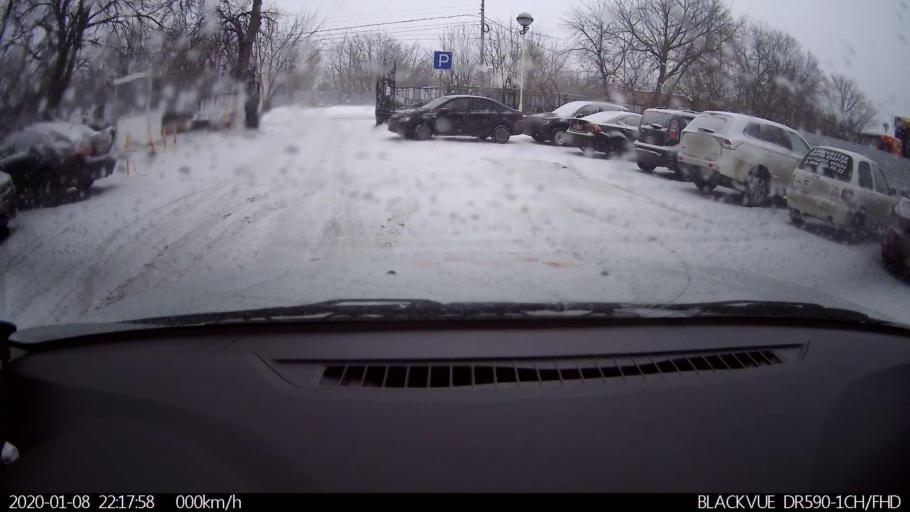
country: RU
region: Nizjnij Novgorod
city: Gorbatovka
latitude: 56.2437
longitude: 43.8696
